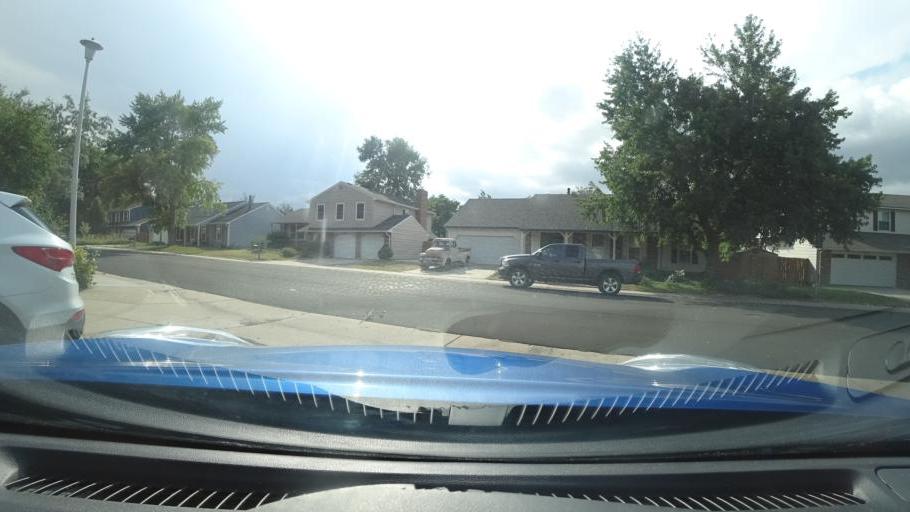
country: US
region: Colorado
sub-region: Adams County
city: Aurora
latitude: 39.6911
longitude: -104.8010
